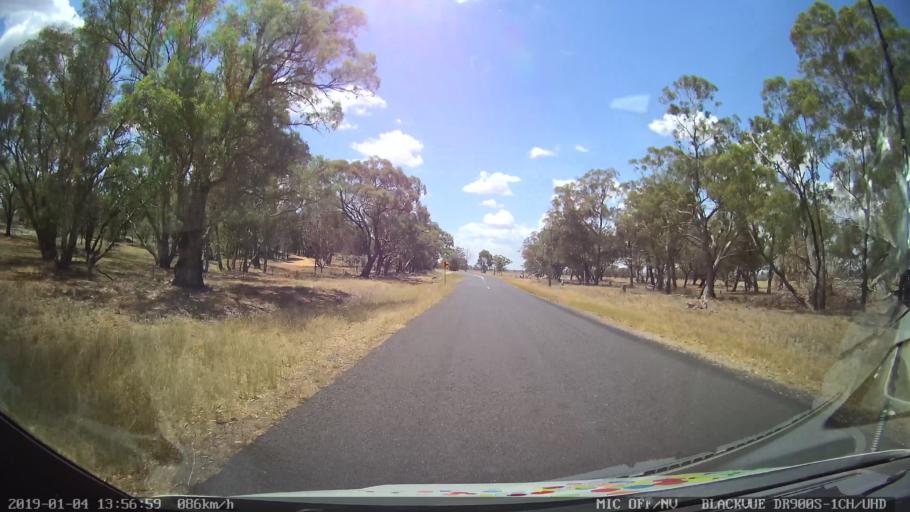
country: AU
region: New South Wales
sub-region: Dubbo Municipality
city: Dubbo
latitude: -32.3454
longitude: 148.5985
